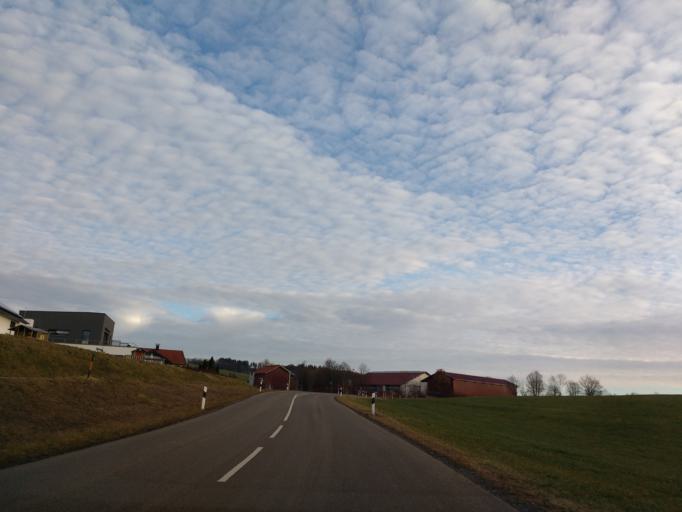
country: DE
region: Bavaria
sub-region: Swabia
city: Neuburg
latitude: 47.7768
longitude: 10.3587
